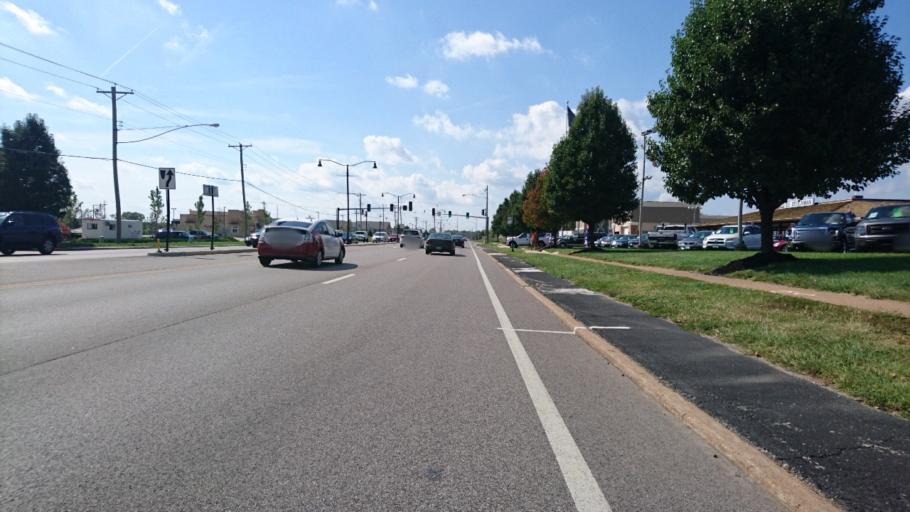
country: US
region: Missouri
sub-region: Saint Louis County
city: Ellisville
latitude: 38.5928
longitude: -90.5760
